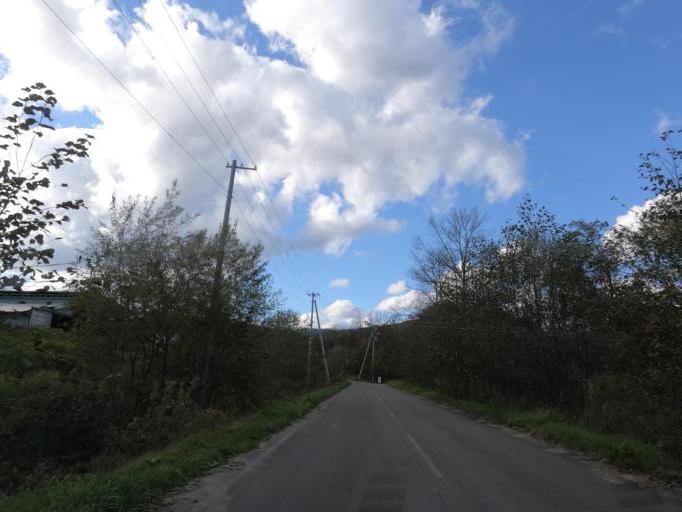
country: JP
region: Hokkaido
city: Otofuke
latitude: 43.2904
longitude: 143.2276
